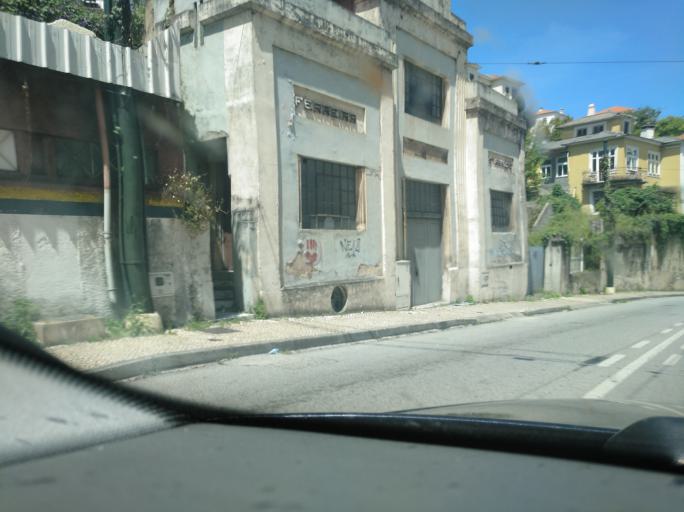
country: PT
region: Coimbra
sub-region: Coimbra
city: Coimbra
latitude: 40.2030
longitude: -8.4185
